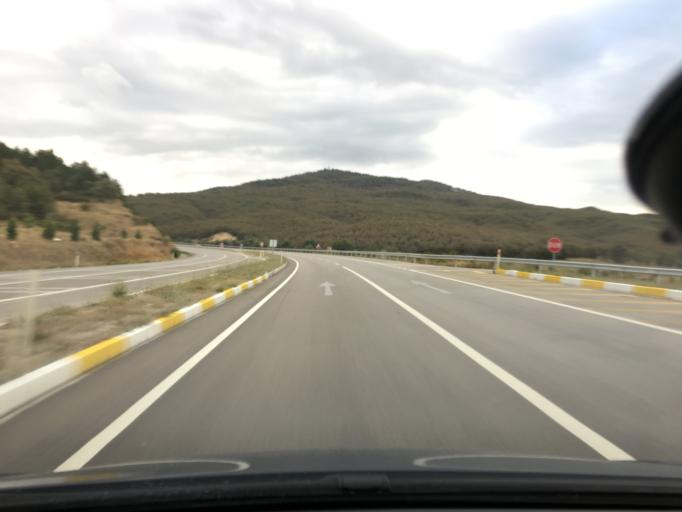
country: TR
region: Afyonkarahisar
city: Sincanli
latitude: 38.7095
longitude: 30.3191
